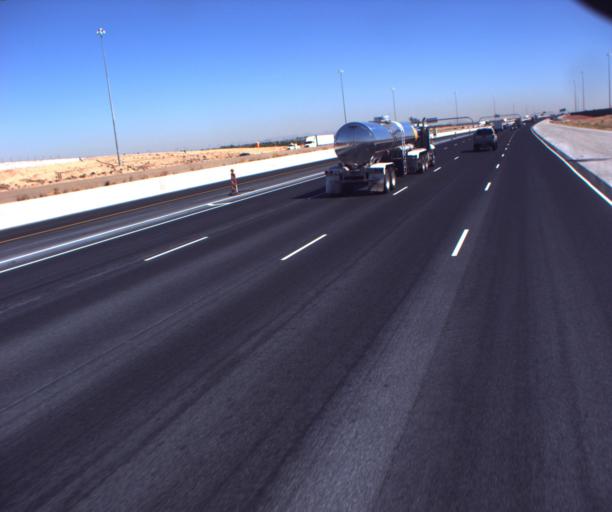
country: US
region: Arizona
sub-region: Maricopa County
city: Goodyear
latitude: 33.4617
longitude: -112.4218
